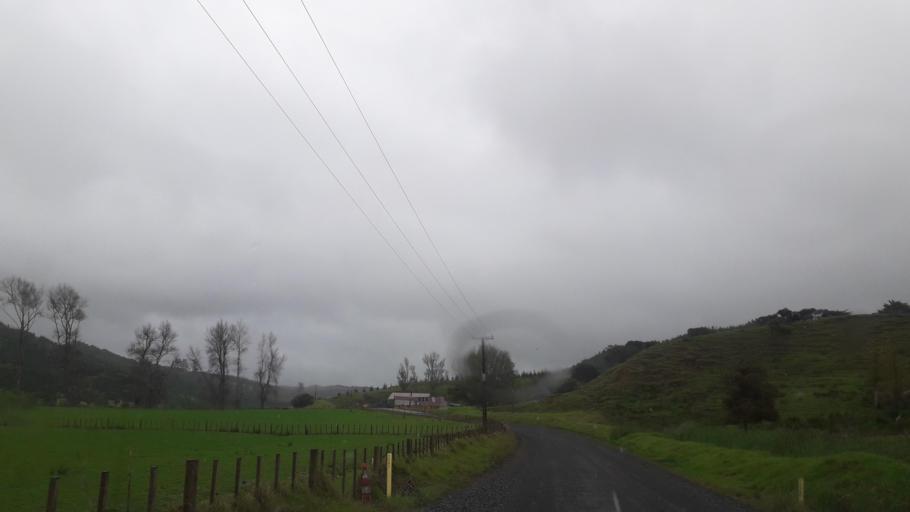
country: NZ
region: Northland
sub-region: Far North District
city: Ahipara
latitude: -35.4235
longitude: 173.3590
